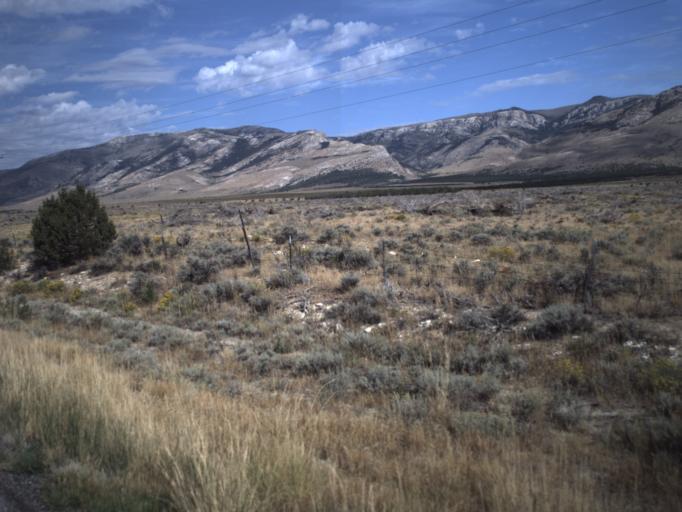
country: US
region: Idaho
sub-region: Cassia County
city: Burley
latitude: 41.8166
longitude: -113.3903
